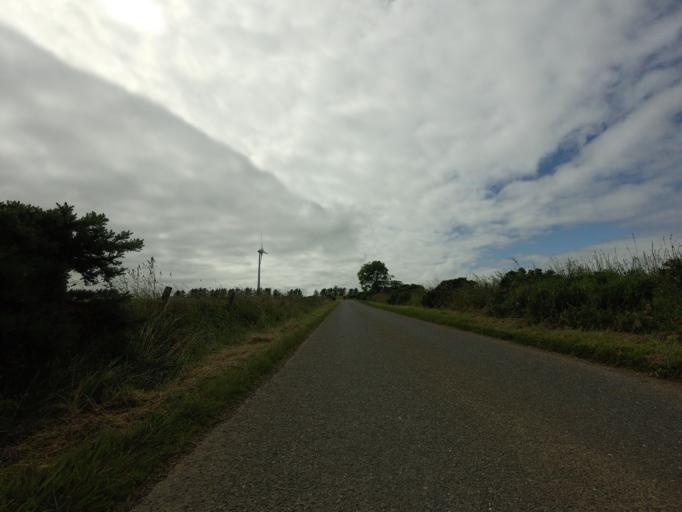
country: GB
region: Scotland
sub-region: Aberdeenshire
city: Turriff
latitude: 57.5455
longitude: -2.2898
